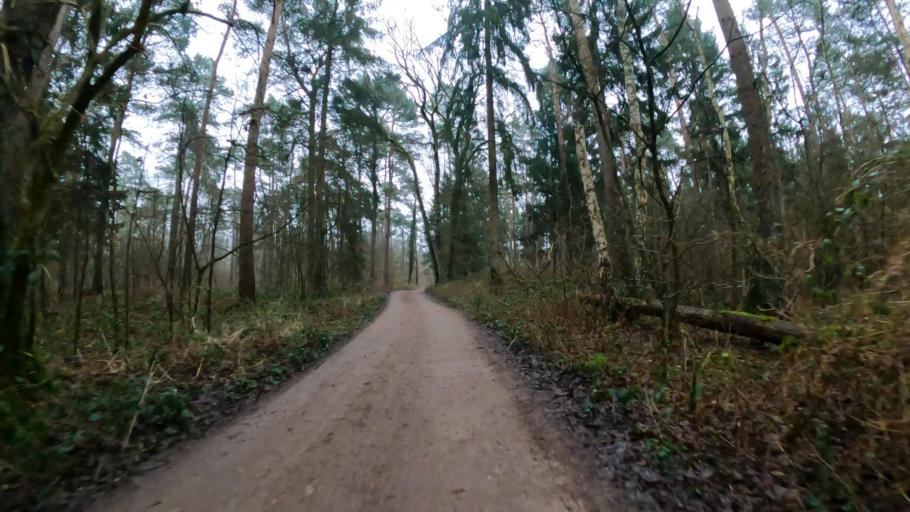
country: DE
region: Schleswig-Holstein
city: Wedel
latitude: 53.5951
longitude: 9.7390
